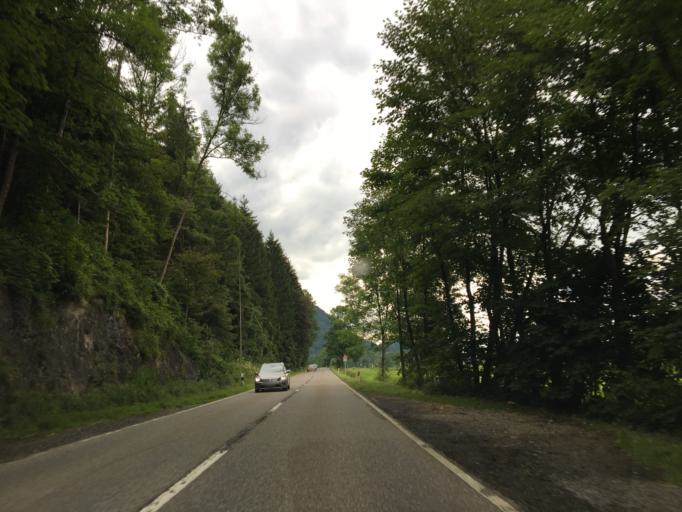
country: AT
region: Tyrol
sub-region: Politischer Bezirk Kufstein
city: Erl
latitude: 47.6733
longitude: 12.1638
